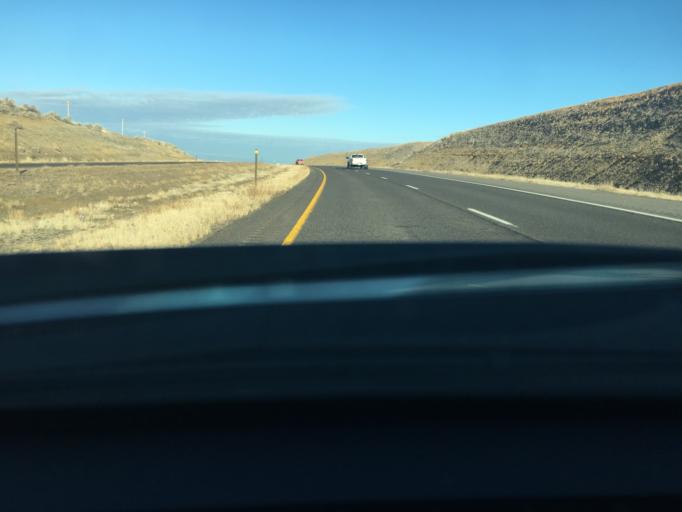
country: US
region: Colorado
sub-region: Mesa County
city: Clifton
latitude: 38.9237
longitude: -108.3823
